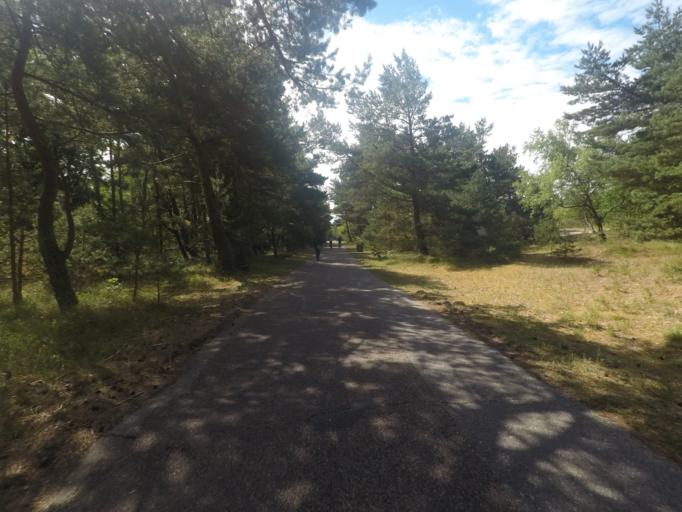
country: LT
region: Klaipedos apskritis
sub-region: Klaipeda
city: Klaipeda
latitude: 55.5509
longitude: 21.1017
